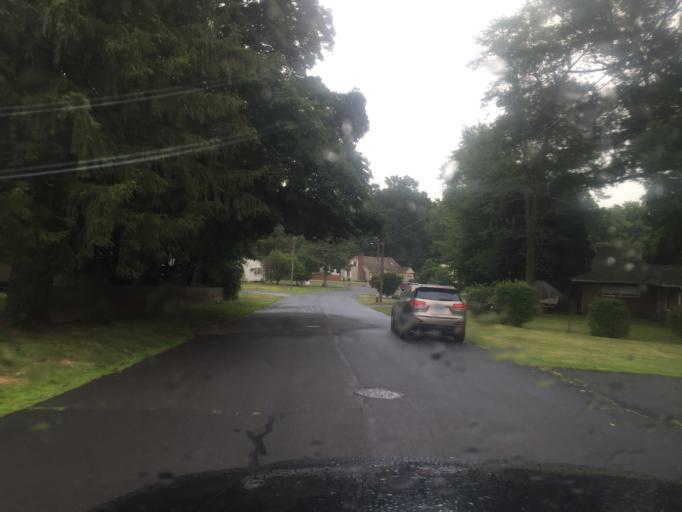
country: US
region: Connecticut
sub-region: Hartford County
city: New Britain
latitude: 41.6978
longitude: -72.7671
